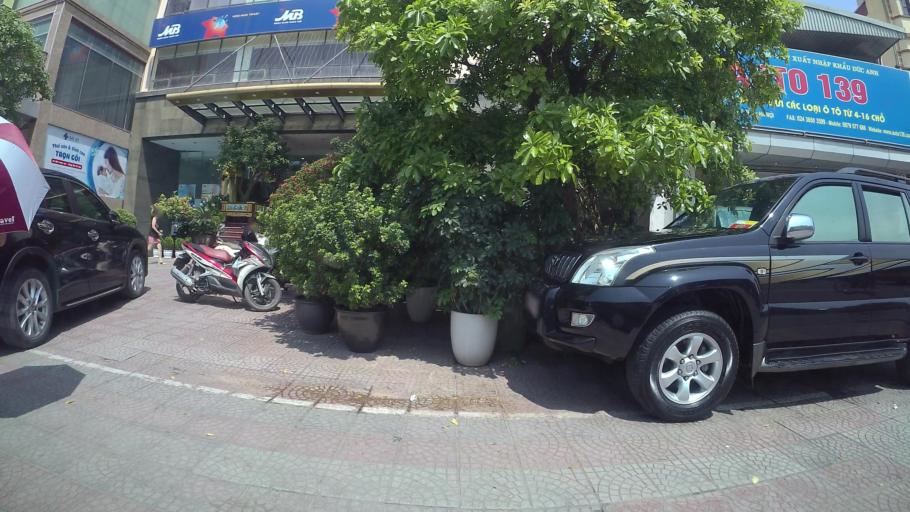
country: VN
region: Ha Noi
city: Hoan Kiem
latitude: 21.0431
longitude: 105.8712
